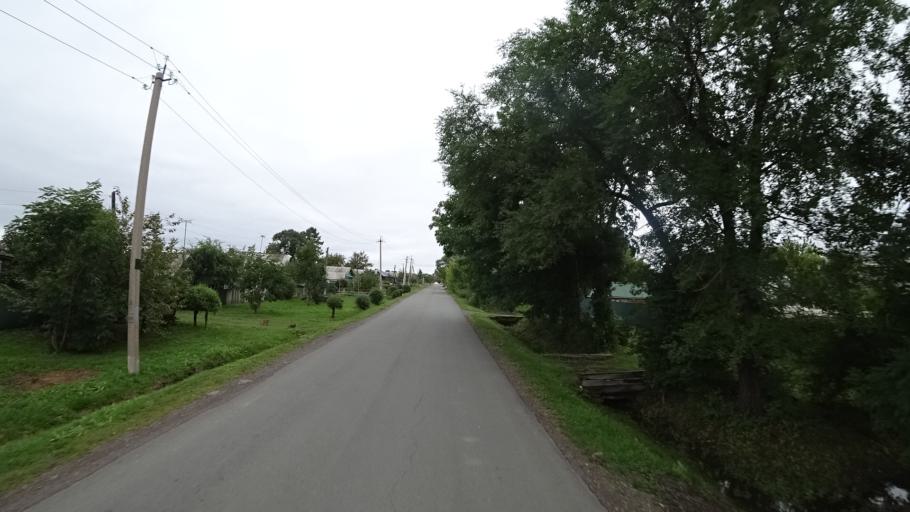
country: RU
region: Primorskiy
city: Chernigovka
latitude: 44.3492
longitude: 132.5663
